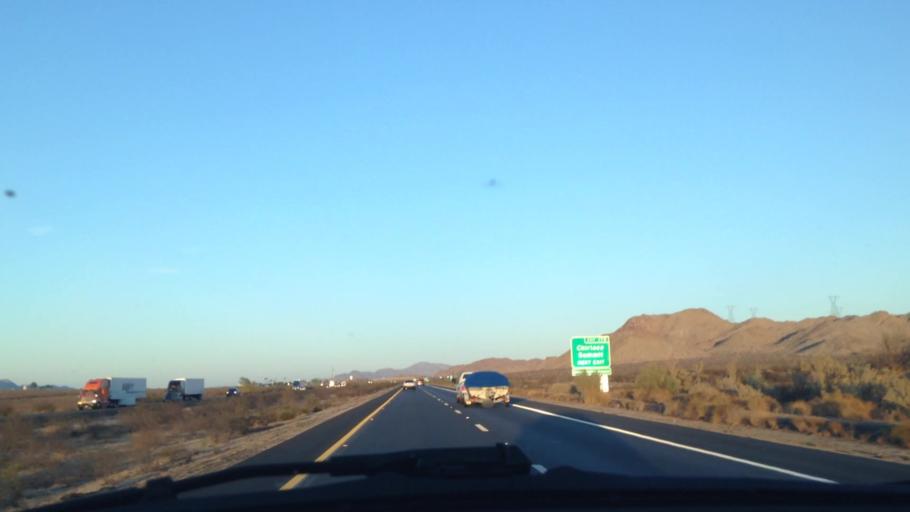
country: US
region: California
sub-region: Riverside County
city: Mecca
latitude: 33.6589
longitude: -115.7401
